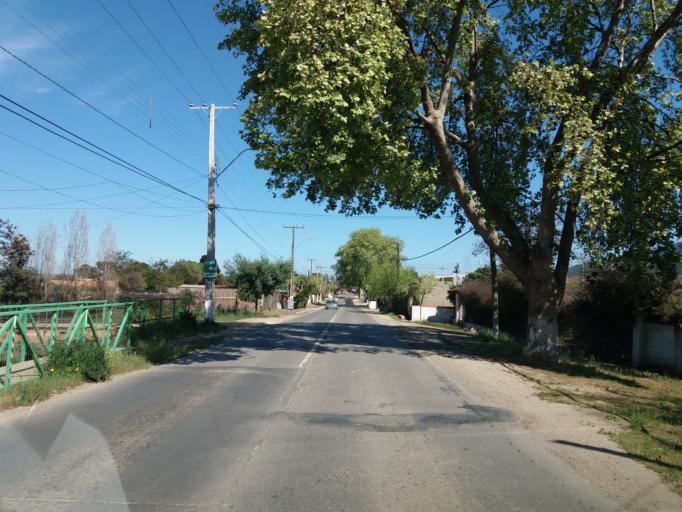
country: CL
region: Valparaiso
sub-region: Provincia de Marga Marga
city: Limache
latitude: -33.0006
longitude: -71.2073
